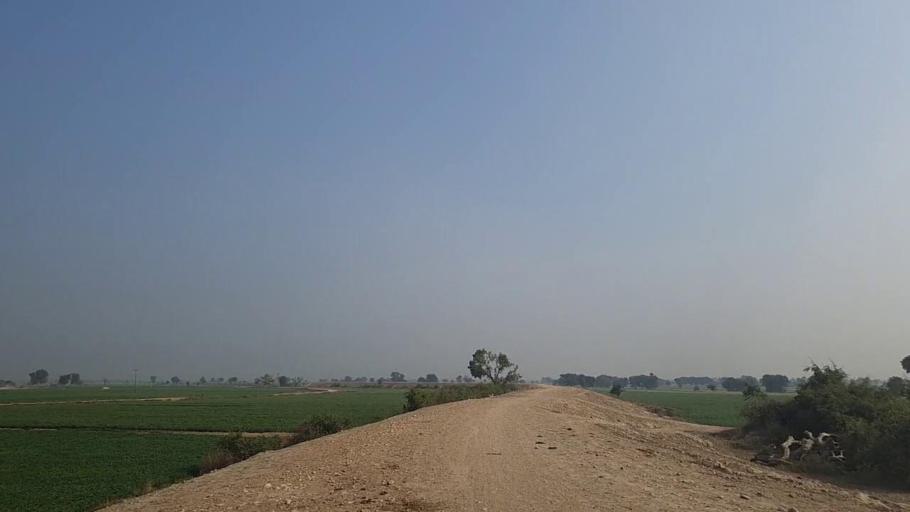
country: PK
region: Sindh
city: Sann
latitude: 26.0882
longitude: 68.1557
